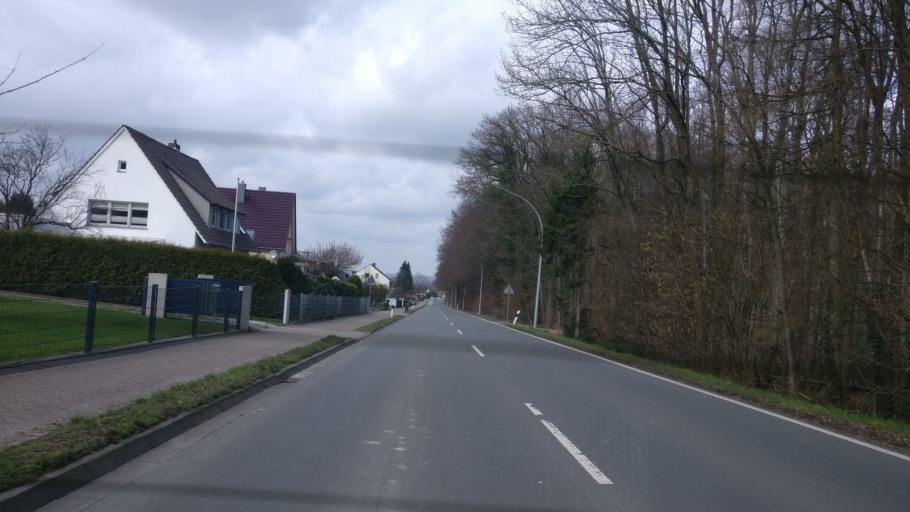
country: DE
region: North Rhine-Westphalia
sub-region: Regierungsbezirk Detmold
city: Lage
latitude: 52.0059
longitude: 8.7957
